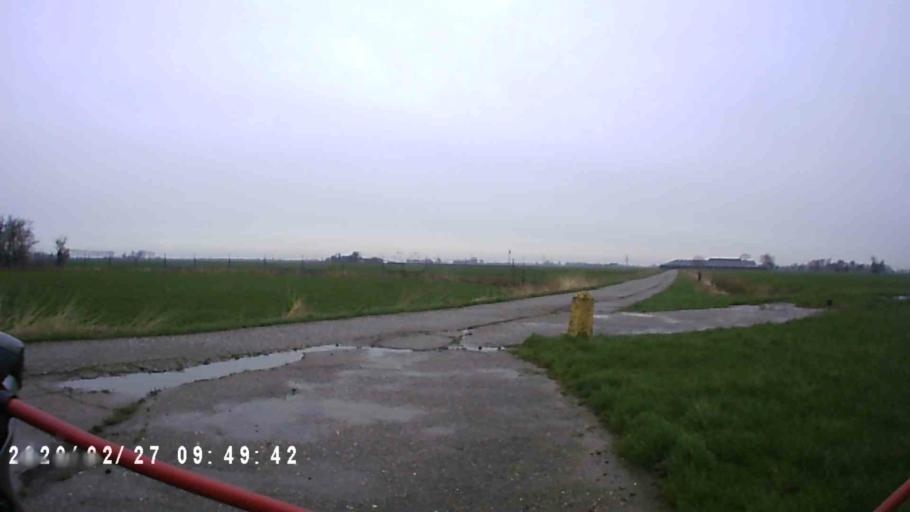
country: NL
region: Groningen
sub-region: Gemeente Zuidhorn
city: Aduard
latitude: 53.2713
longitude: 6.4549
